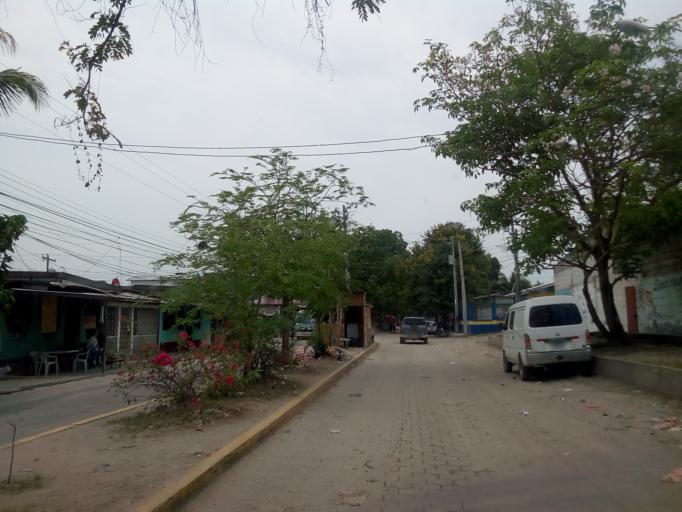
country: HN
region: Cortes
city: La Lima
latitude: 15.4589
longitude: -87.9483
